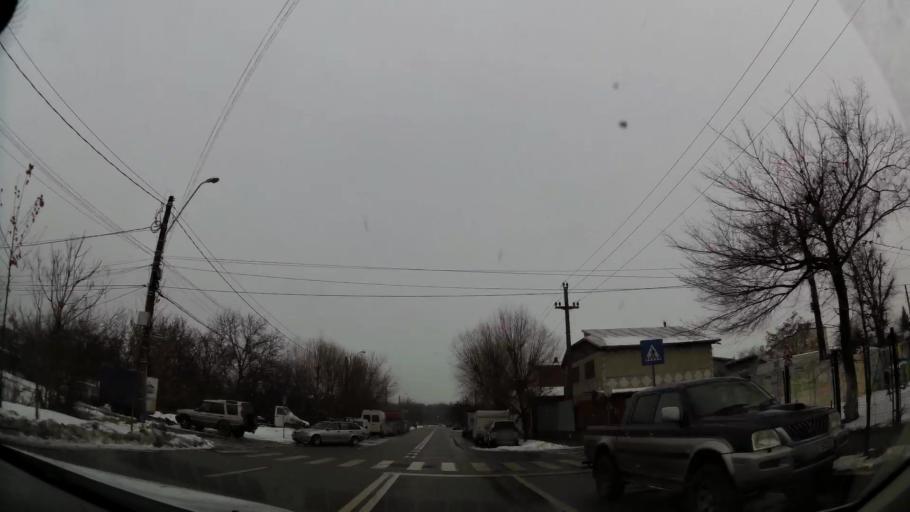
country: RO
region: Ilfov
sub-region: Comuna Mogosoaia
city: Mogosoaia
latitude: 44.5109
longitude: 26.0159
